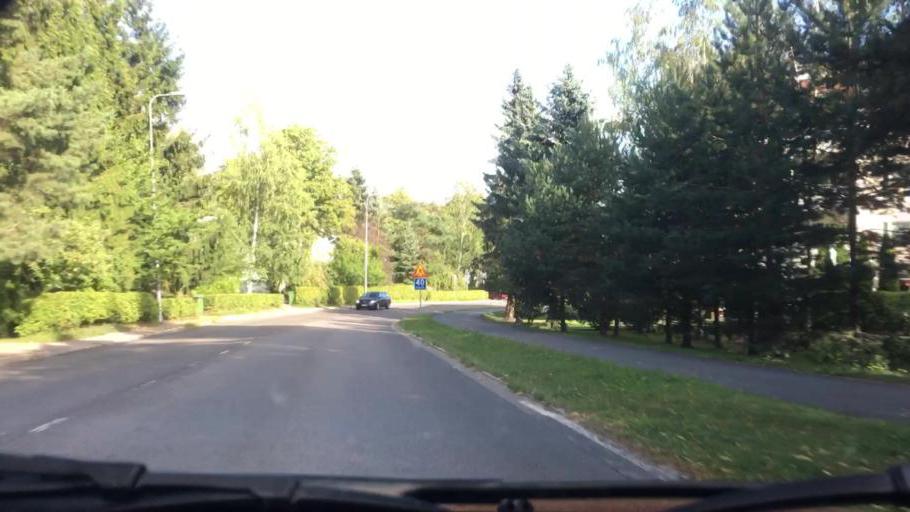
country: FI
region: Varsinais-Suomi
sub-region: Turku
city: Turku
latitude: 60.4649
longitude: 22.2403
